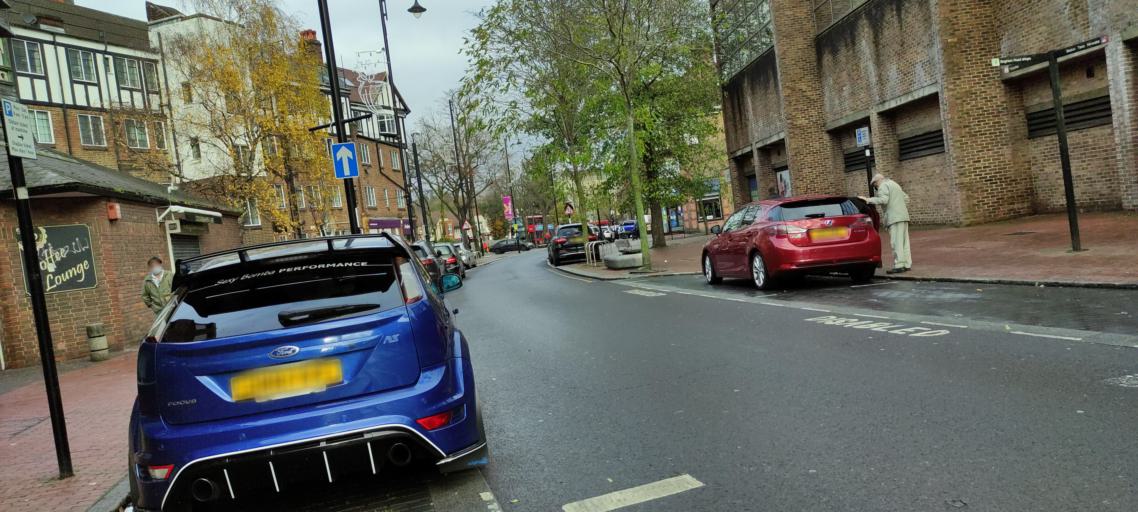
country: GB
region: England
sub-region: Greater London
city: Purley
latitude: 51.3389
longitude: -0.1153
